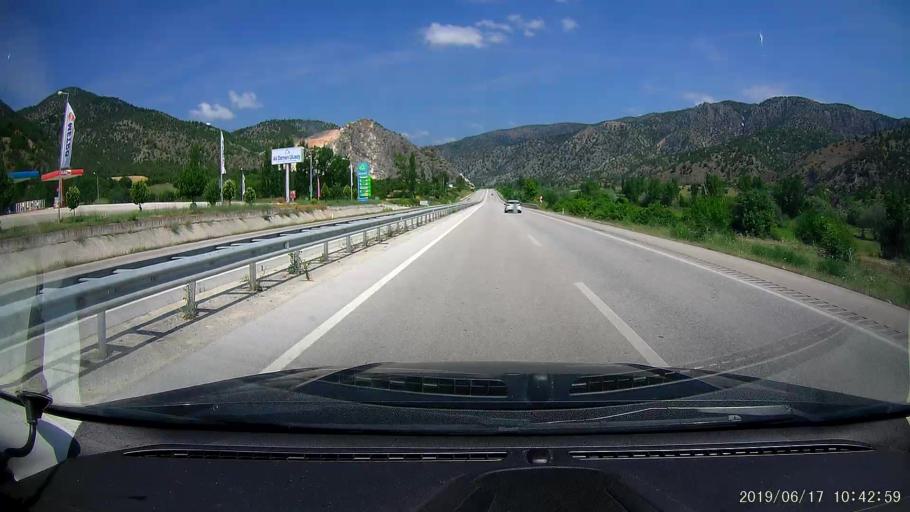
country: TR
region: Corum
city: Kargi
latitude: 41.0563
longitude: 34.5435
